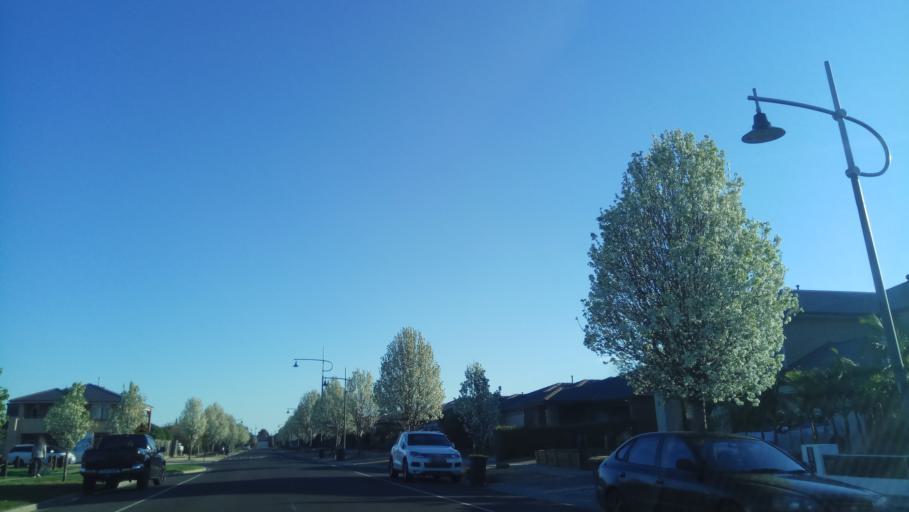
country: AU
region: Victoria
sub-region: Wyndham
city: Point Cook
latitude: -37.9079
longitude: 144.7372
